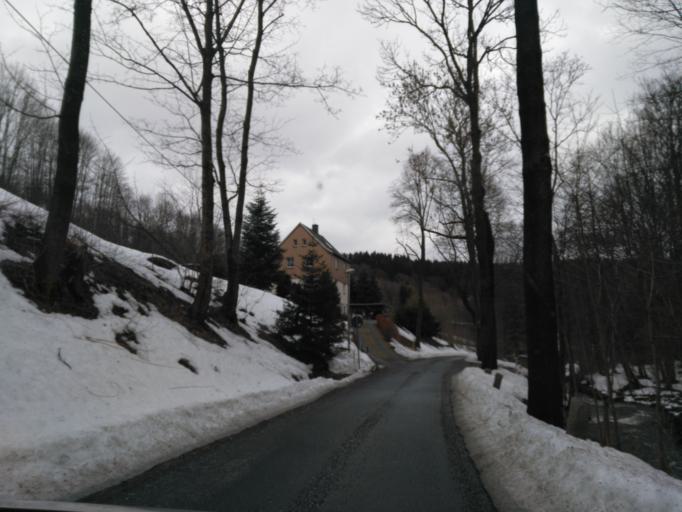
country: DE
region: Saxony
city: Barenstein
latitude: 50.5082
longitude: 13.0306
